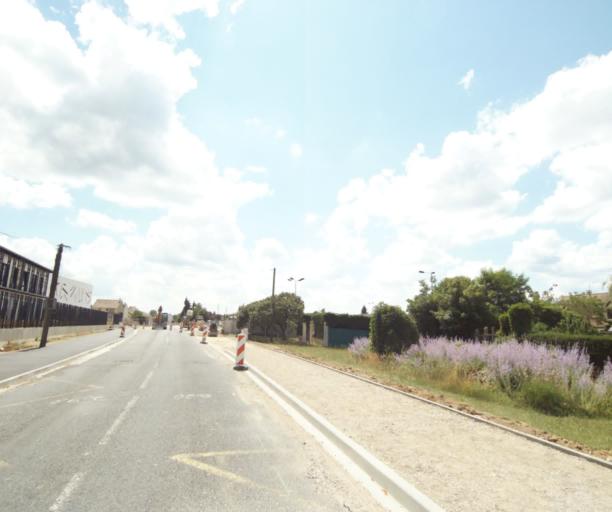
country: FR
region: Ile-de-France
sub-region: Departement de Seine-et-Marne
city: Samoreau
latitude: 48.4397
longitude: 2.7560
